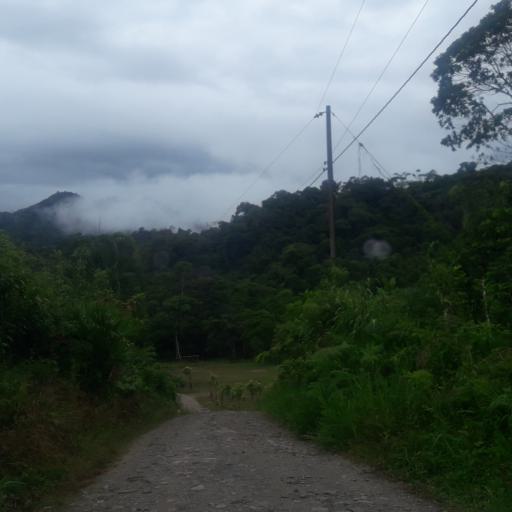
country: EC
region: Napo
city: Archidona
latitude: -0.9110
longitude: -77.8250
